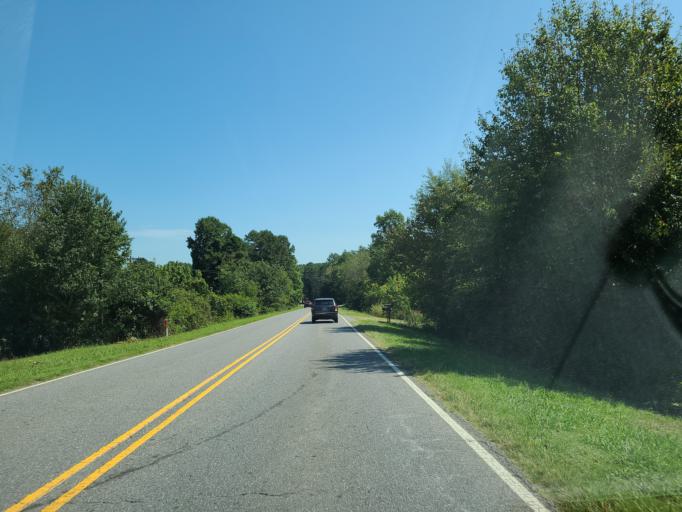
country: US
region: North Carolina
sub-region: Cleveland County
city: Shelby
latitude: 35.3205
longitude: -81.4785
